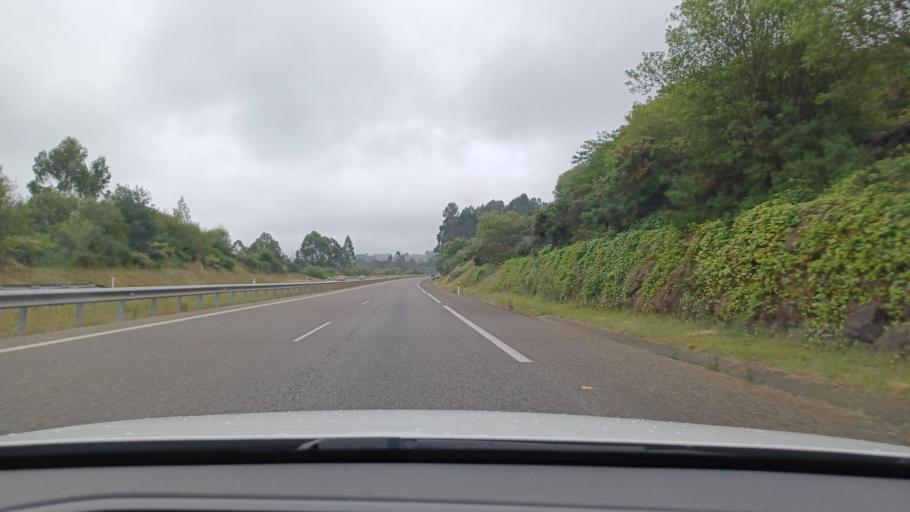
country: ES
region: Asturias
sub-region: Province of Asturias
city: Lugones
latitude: 43.4536
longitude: -5.7847
